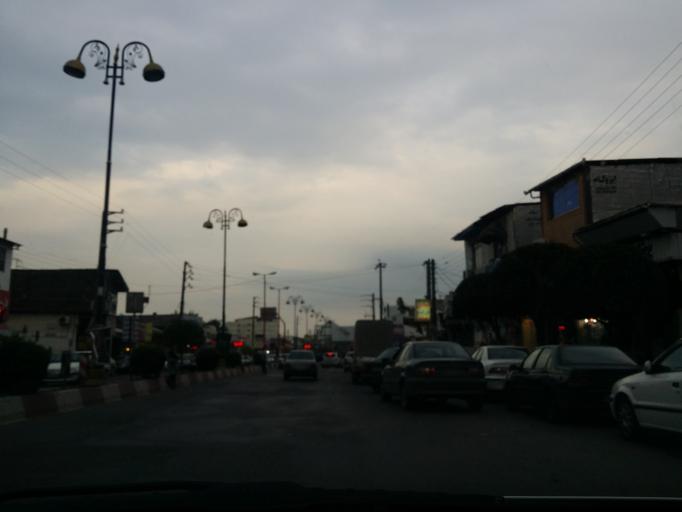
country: IR
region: Mazandaran
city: `Abbasabad
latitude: 36.7288
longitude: 51.1066
